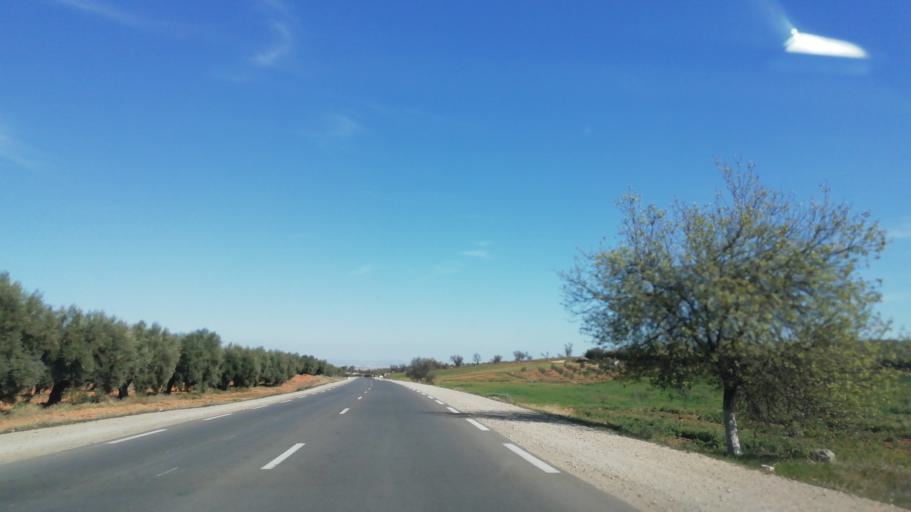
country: DZ
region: Mascara
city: Oued el Abtal
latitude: 35.4264
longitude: 0.4627
